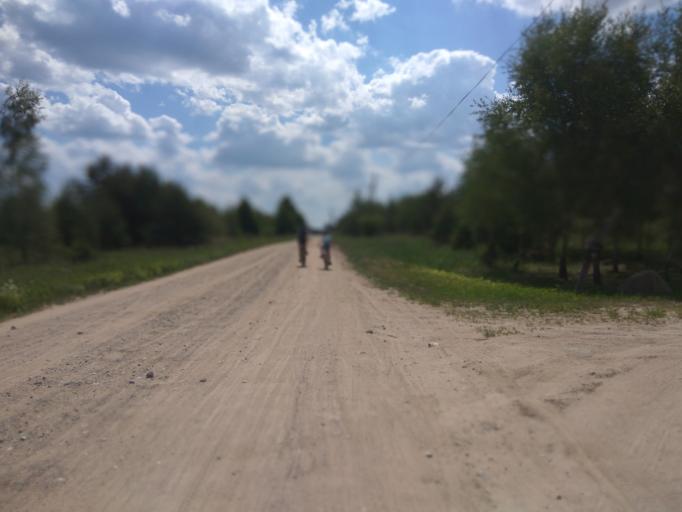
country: LV
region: Kuldigas Rajons
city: Kuldiga
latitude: 56.8986
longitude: 21.9678
